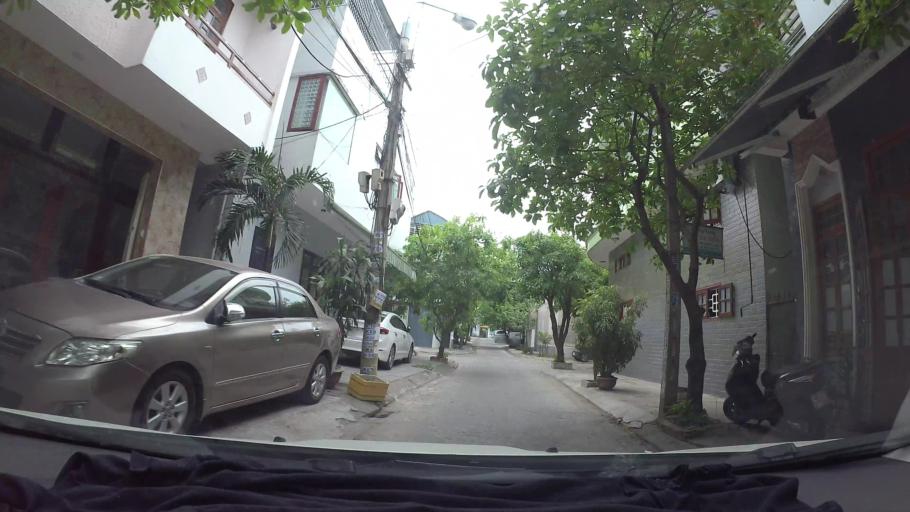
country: VN
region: Da Nang
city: Thanh Khe
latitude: 16.0640
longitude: 108.1900
